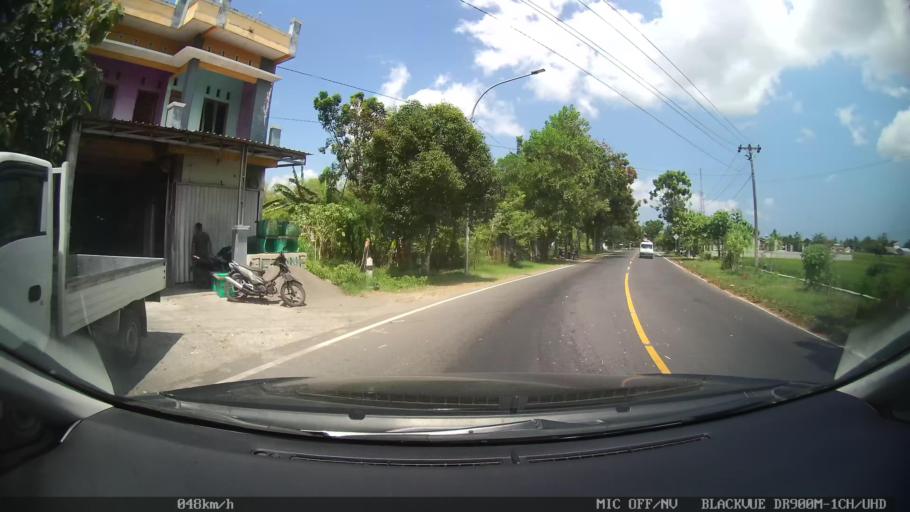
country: ID
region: Daerah Istimewa Yogyakarta
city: Sewon
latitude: -7.8831
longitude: 110.3469
